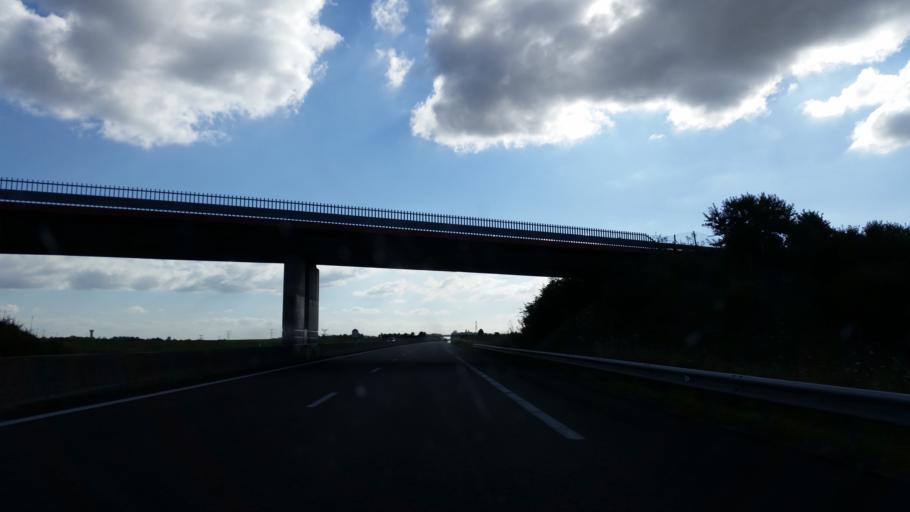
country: FR
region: Picardie
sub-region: Departement de la Somme
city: Beaucamps-le-Vieux
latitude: 49.7996
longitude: 1.8074
